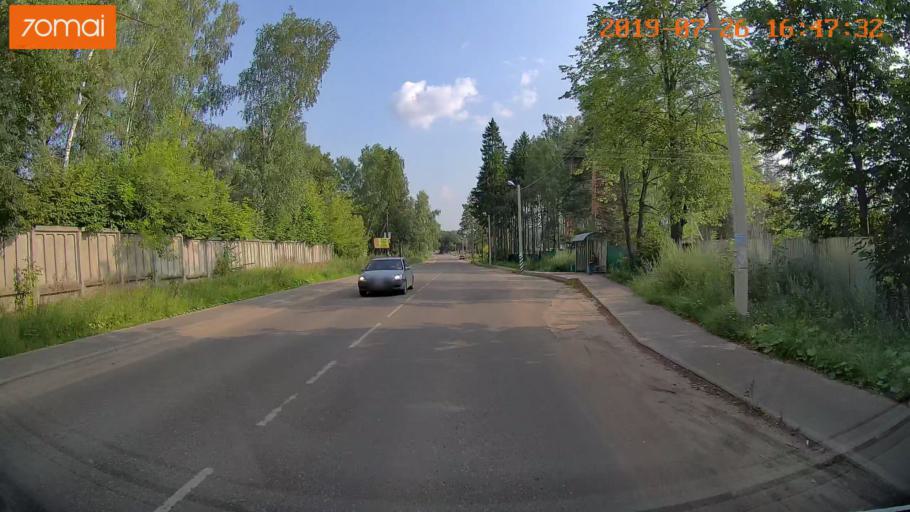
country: RU
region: Ivanovo
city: Bogorodskoye
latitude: 57.0406
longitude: 41.0122
